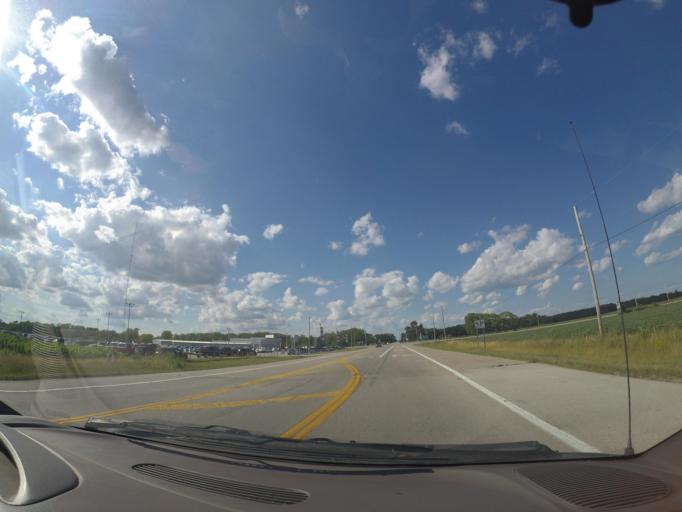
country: US
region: Ohio
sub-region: Sandusky County
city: Woodville
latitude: 41.4701
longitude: -83.4150
